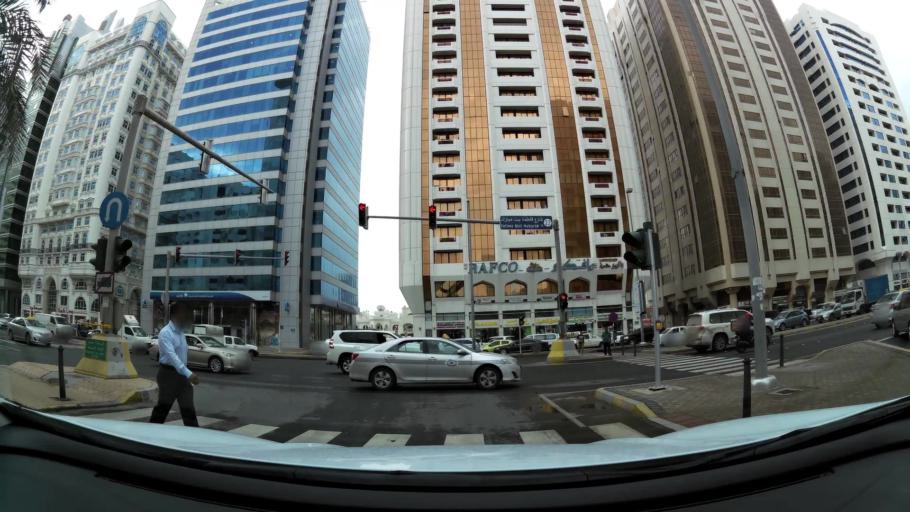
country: AE
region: Abu Dhabi
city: Abu Dhabi
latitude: 24.4883
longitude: 54.3719
